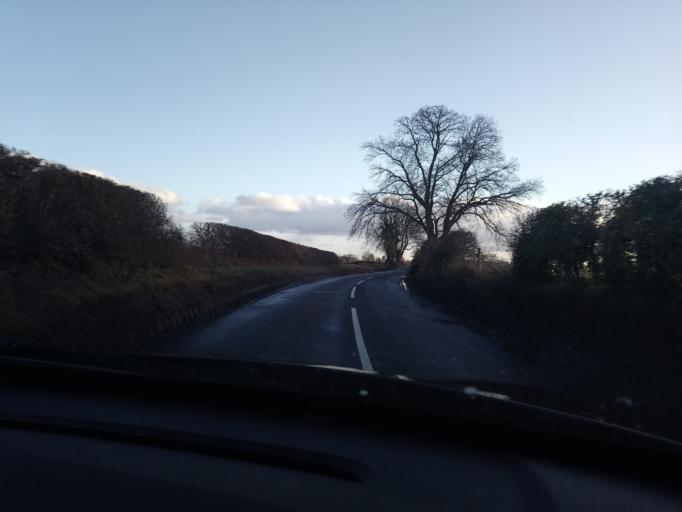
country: GB
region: England
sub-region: Shropshire
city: Petton
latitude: 52.8810
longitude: -2.7854
